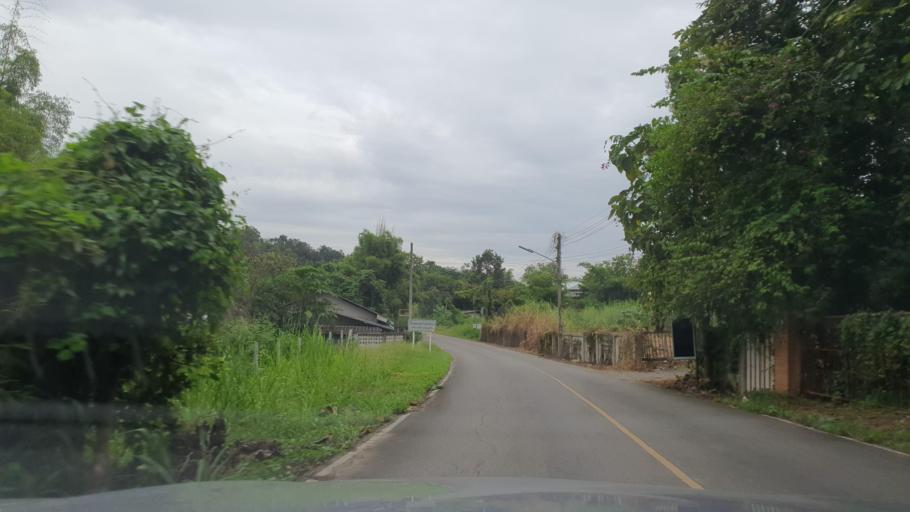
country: TH
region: Chiang Mai
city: San Sai
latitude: 18.9281
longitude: 98.9313
